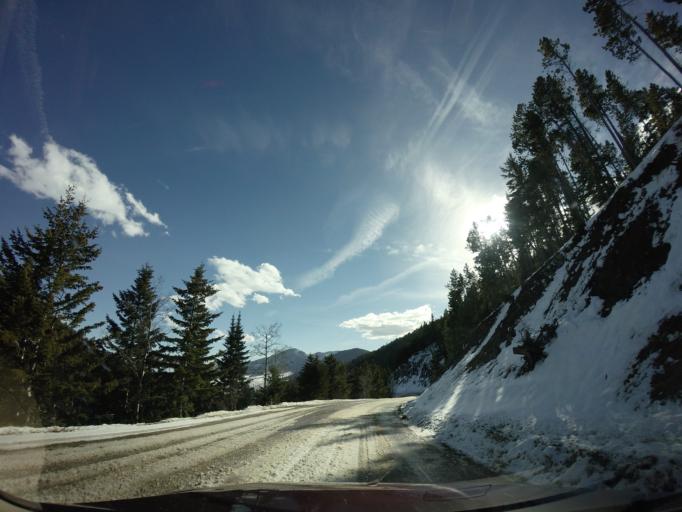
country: US
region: Montana
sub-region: Carbon County
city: Red Lodge
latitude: 45.1779
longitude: -109.3185
